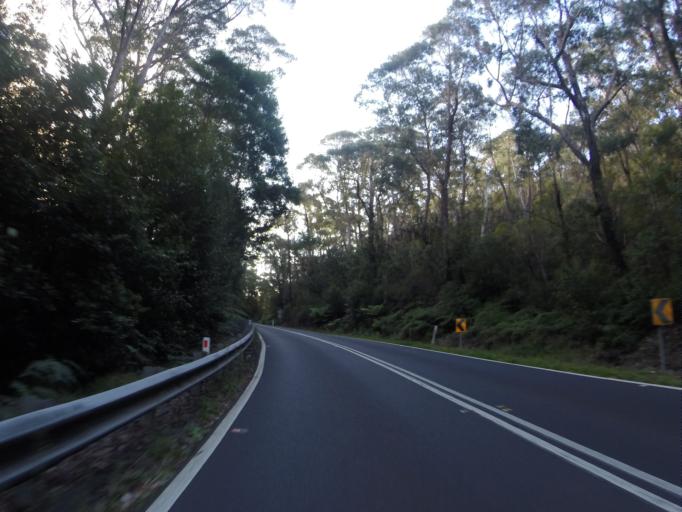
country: AU
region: New South Wales
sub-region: Shoalhaven Shire
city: Kangaroo Valley
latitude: -34.6837
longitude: 150.4900
